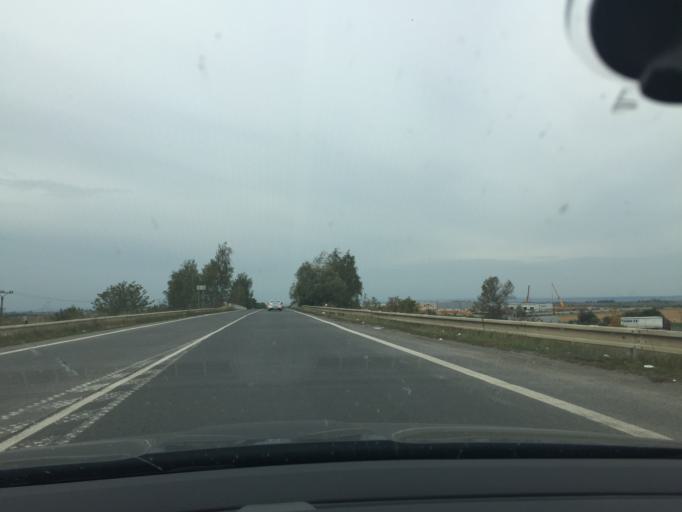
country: CZ
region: Praha
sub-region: Praha 20
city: Horni Pocernice
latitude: 50.1260
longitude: 14.6227
